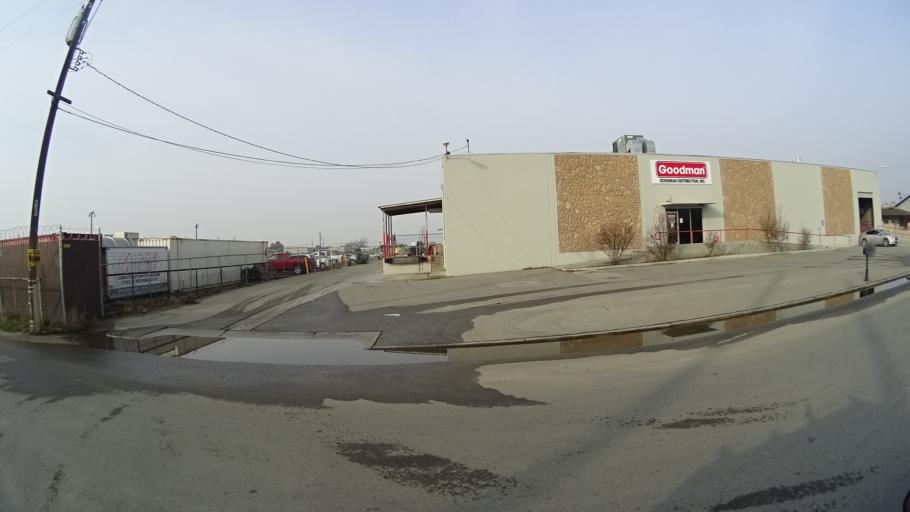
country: US
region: California
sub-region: Kern County
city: Bakersfield
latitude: 35.3859
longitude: -119.0521
